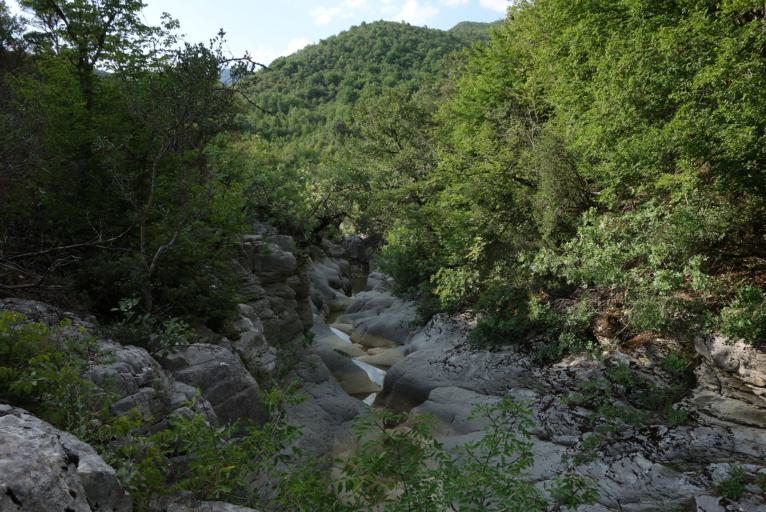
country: AL
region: Gjirokaster
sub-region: Rrethi i Permetit
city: Petran
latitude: 40.2528
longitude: 20.4541
